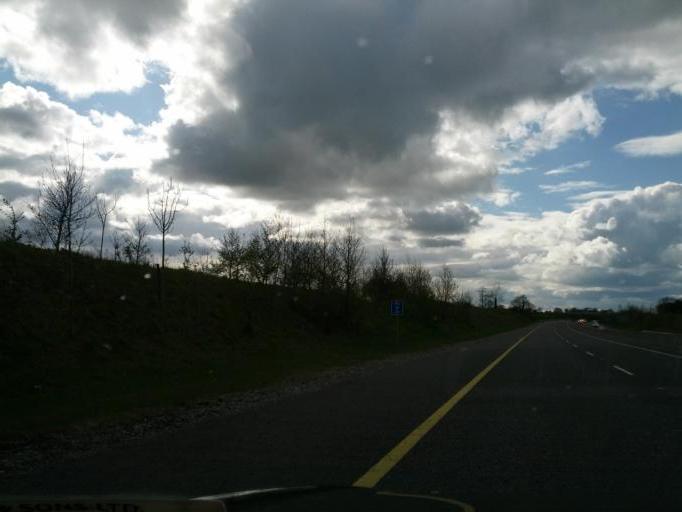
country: IE
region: Leinster
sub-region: An Iarmhi
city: Kilbeggan
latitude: 53.3600
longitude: -7.5113
